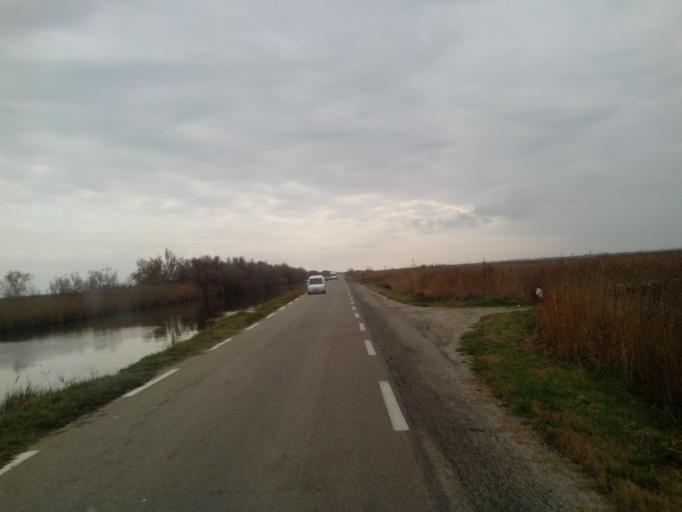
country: FR
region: Languedoc-Roussillon
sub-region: Departement du Gard
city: Vauvert
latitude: 43.6322
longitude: 4.3049
